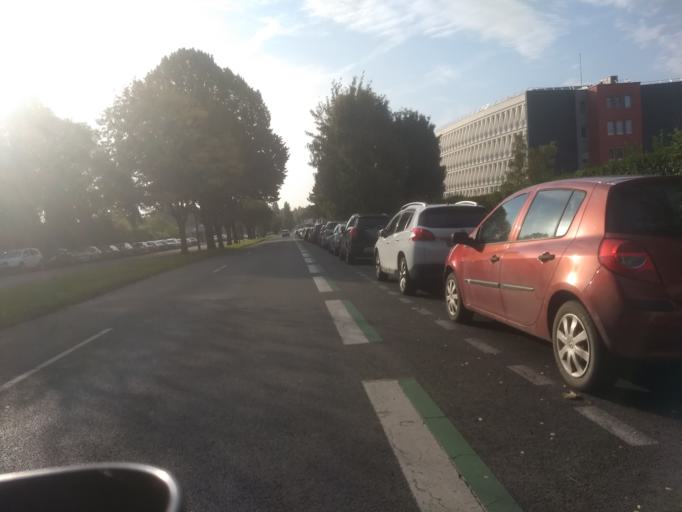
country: FR
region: Nord-Pas-de-Calais
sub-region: Departement du Pas-de-Calais
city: Sainte-Catherine
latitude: 50.2922
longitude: 2.7584
